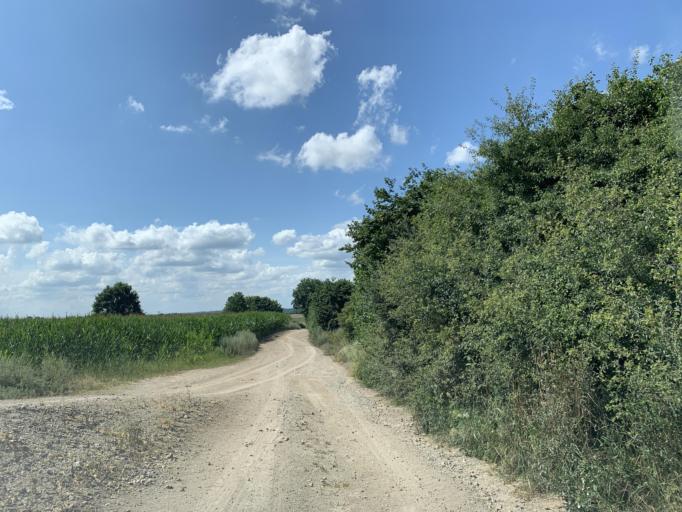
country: DE
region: Mecklenburg-Vorpommern
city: Blankensee
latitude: 53.3965
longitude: 13.2799
